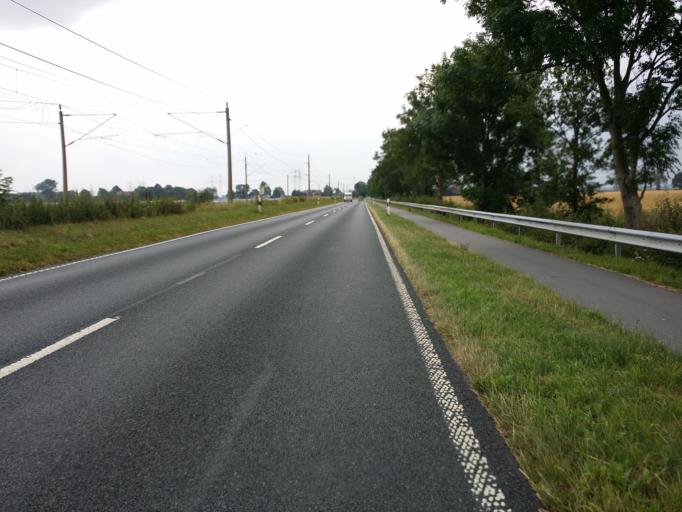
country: DE
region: Schleswig-Holstein
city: Krempermoor
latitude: 53.8645
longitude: 9.4840
